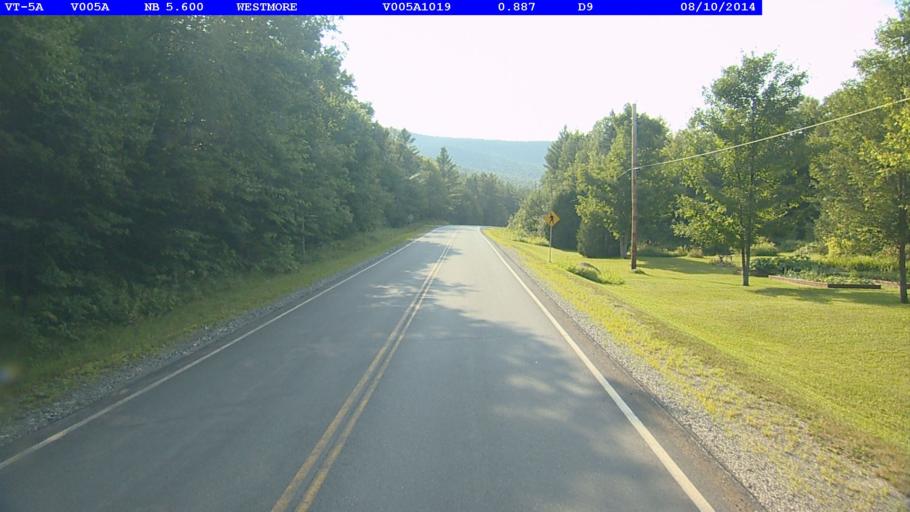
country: US
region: Vermont
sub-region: Caledonia County
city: Lyndonville
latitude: 44.7102
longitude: -72.0218
